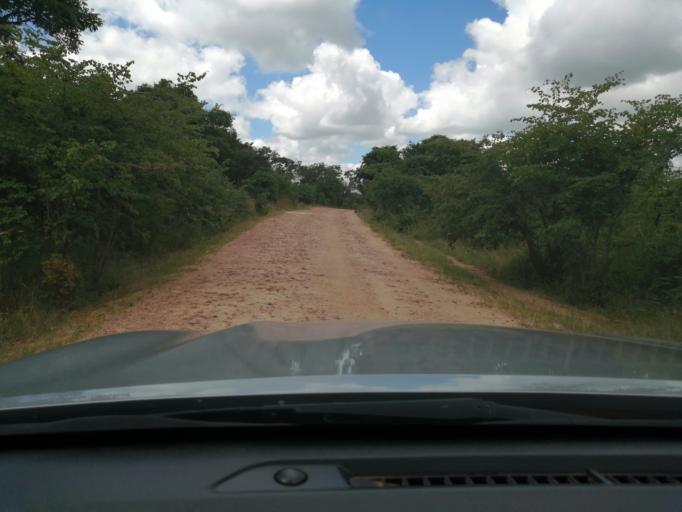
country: ZM
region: Lusaka
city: Lusaka
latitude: -15.1417
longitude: 27.9266
